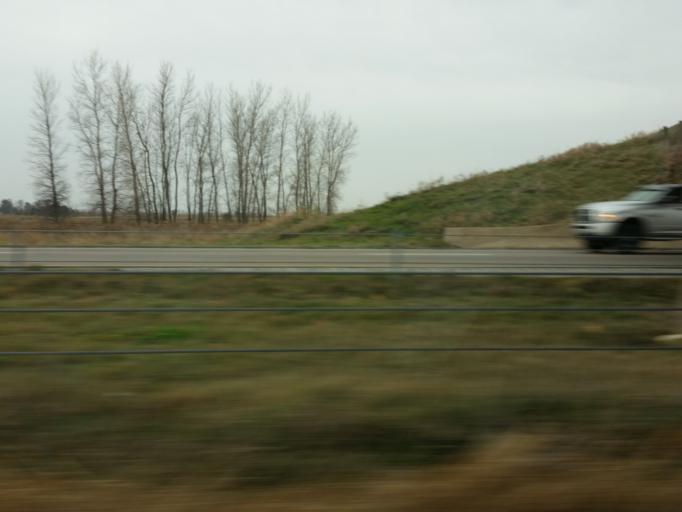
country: US
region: Iowa
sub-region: Scott County
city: Walcott
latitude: 41.6249
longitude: -90.8133
